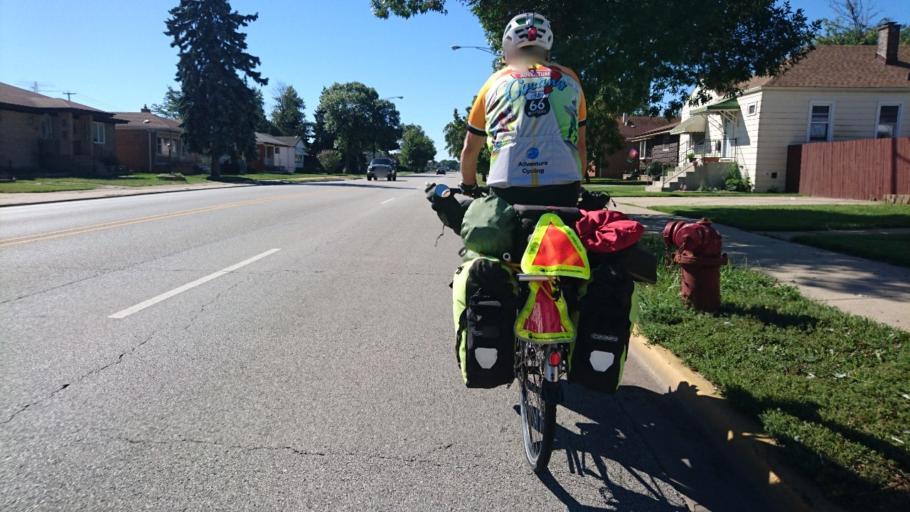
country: US
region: Illinois
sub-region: Cook County
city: Burnham
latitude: 41.6583
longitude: -87.5400
